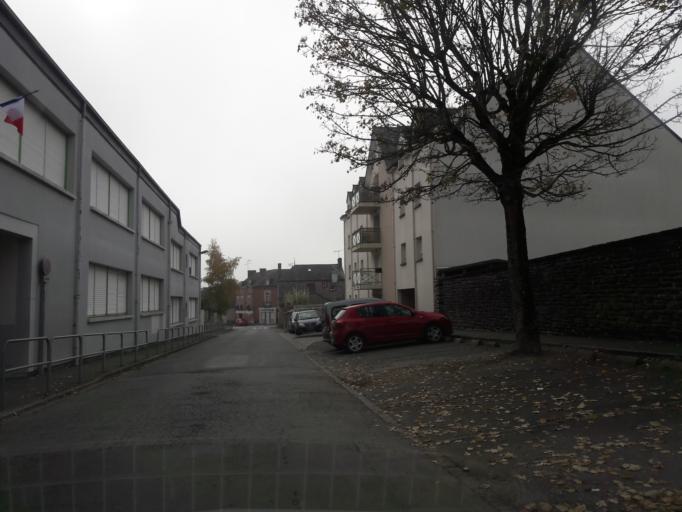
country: FR
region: Brittany
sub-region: Departement d'Ille-et-Vilaine
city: Janze
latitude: 47.9616
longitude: -1.4994
